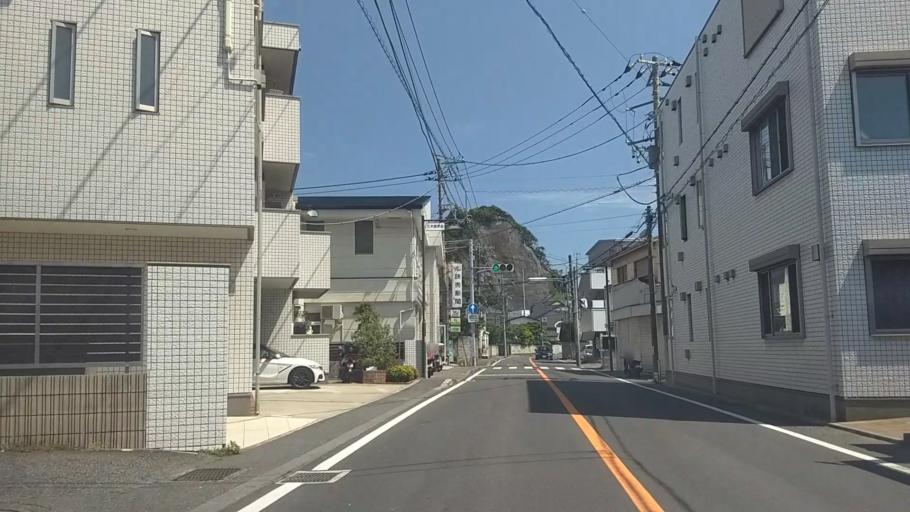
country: JP
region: Kanagawa
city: Zushi
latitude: 35.3001
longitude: 139.5725
